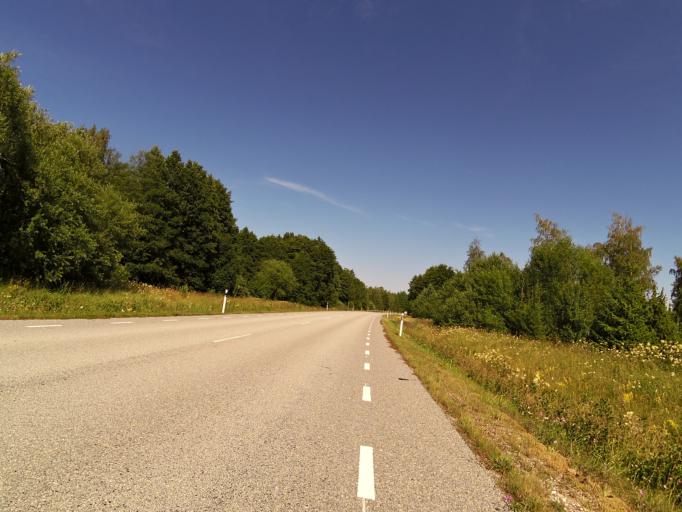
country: EE
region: Hiiumaa
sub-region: Kaerdla linn
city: Kardla
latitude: 58.9996
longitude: 22.5338
